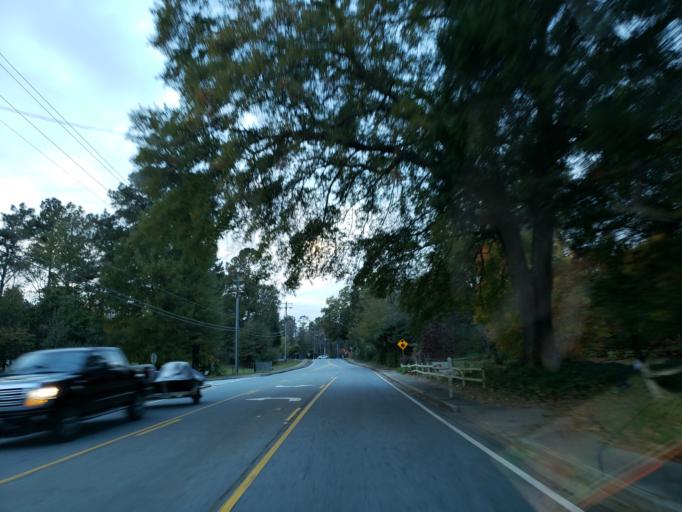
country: US
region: Georgia
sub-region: Cobb County
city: Acworth
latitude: 34.0156
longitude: -84.6732
